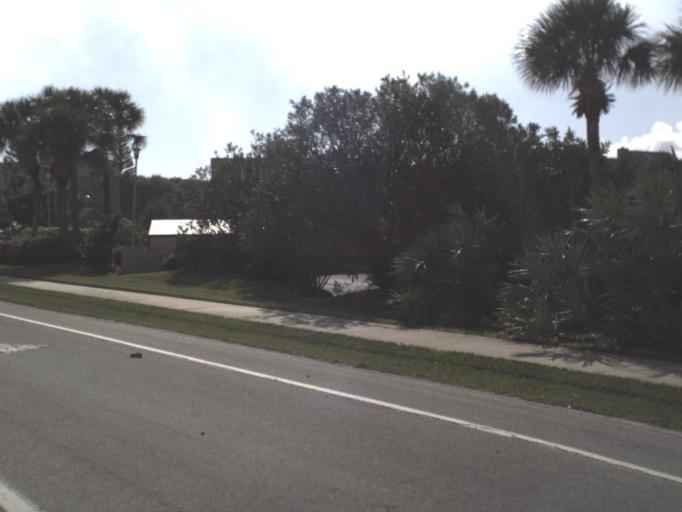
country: US
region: Florida
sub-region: Volusia County
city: Edgewater
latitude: 29.0006
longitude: -80.8741
